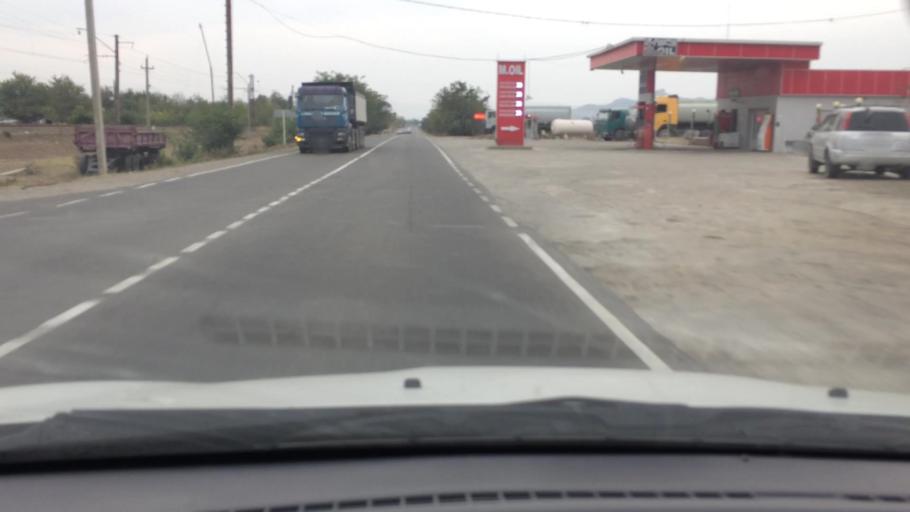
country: GE
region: Kvemo Kartli
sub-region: Marneuli
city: Marneuli
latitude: 41.4301
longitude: 44.8214
